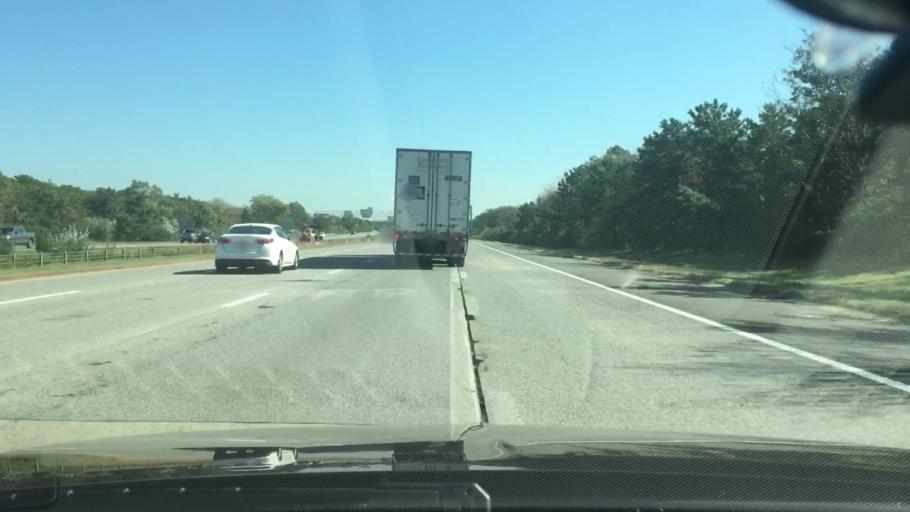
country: US
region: New York
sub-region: Suffolk County
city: Medford
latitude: 40.8231
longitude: -72.9896
